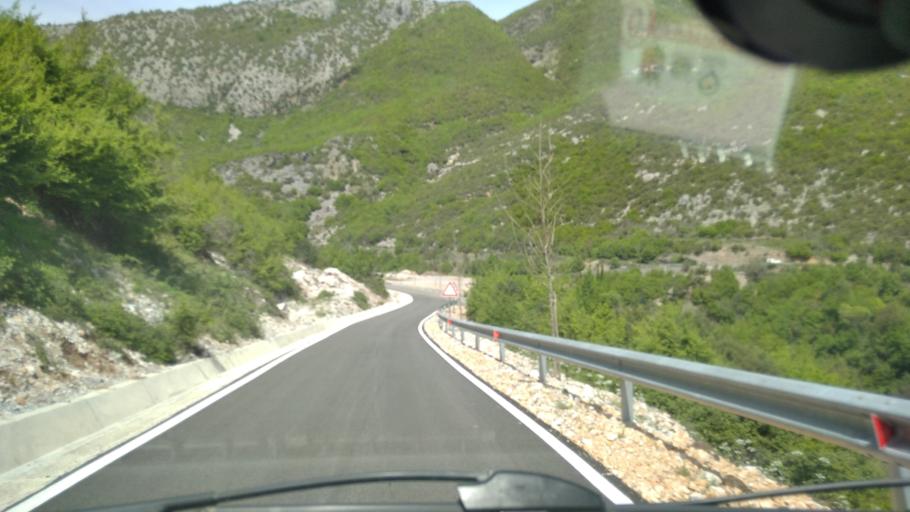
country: AL
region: Shkoder
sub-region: Rrethi i Shkodres
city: Guri i Zi
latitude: 42.1284
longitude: 19.6144
